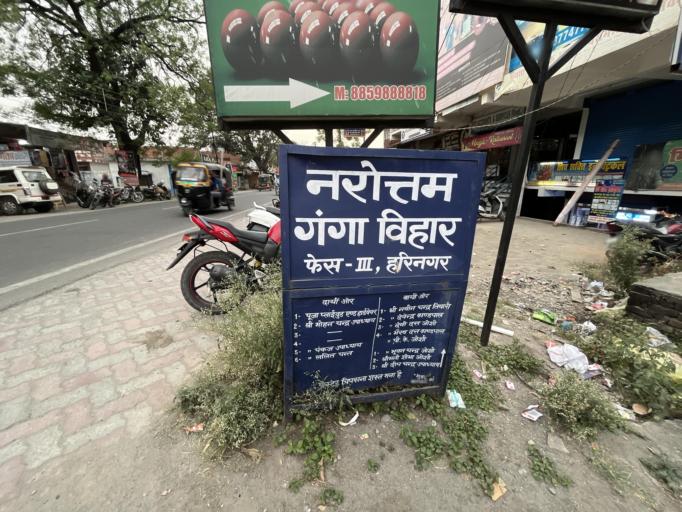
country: IN
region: Uttarakhand
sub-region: Naini Tal
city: Haldwani
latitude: 29.2216
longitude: 79.4999
